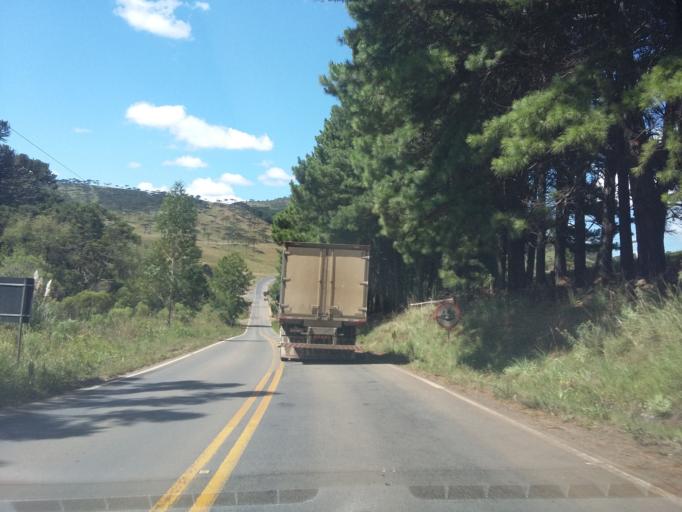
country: BR
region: Santa Catarina
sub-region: Sao Joaquim
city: Sao Joaquim
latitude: -28.3114
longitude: -49.7166
